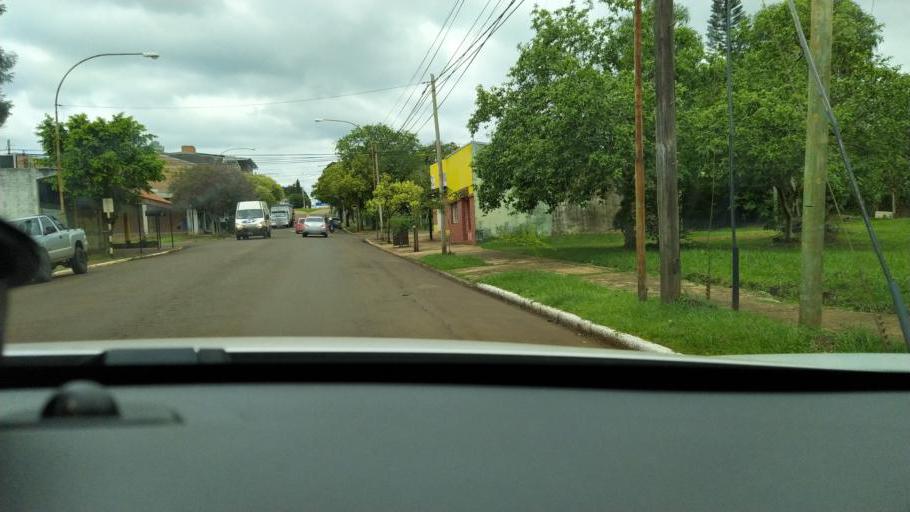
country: AR
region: Misiones
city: Puerto Rico
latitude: -26.8187
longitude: -55.0225
